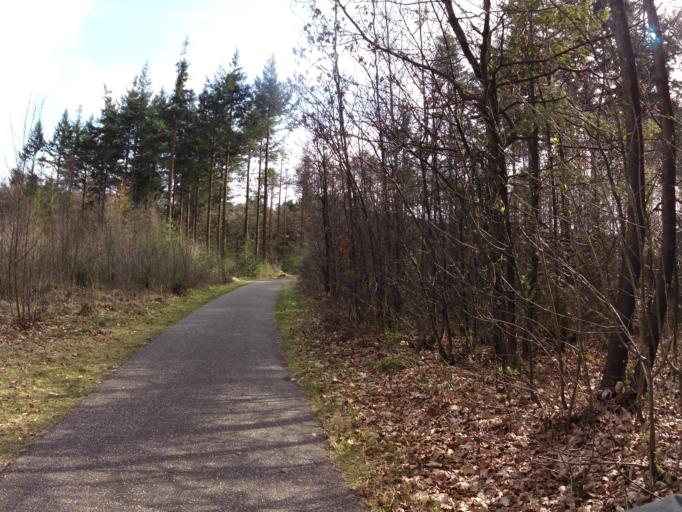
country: NL
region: Friesland
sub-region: Gemeente Weststellingwerf
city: Noordwolde
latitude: 52.8718
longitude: 6.1993
